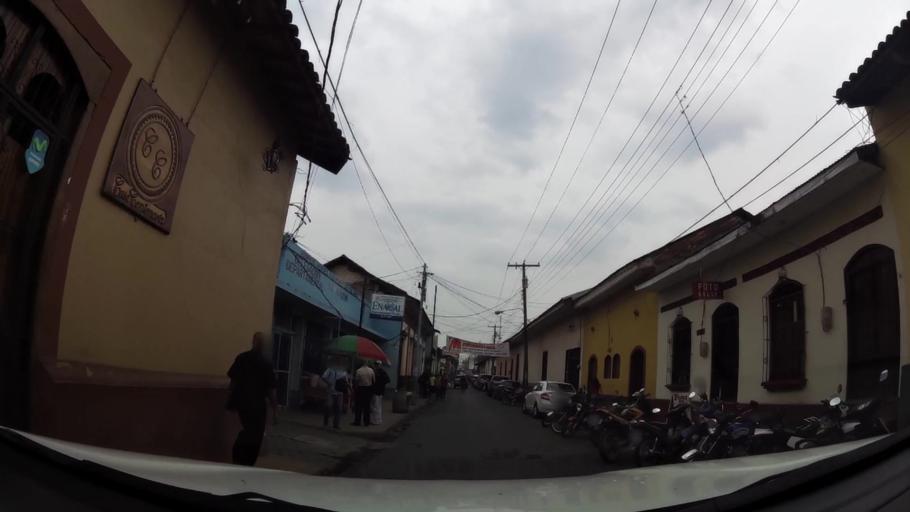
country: NI
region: Leon
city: Leon
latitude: 12.4350
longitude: -86.8750
